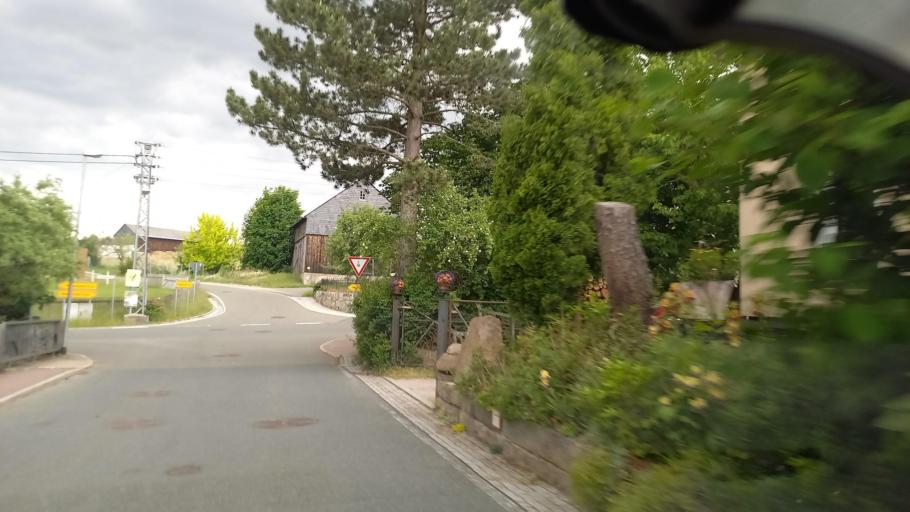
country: DE
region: Saxony
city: Rodewisch
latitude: 50.5558
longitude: 12.4558
